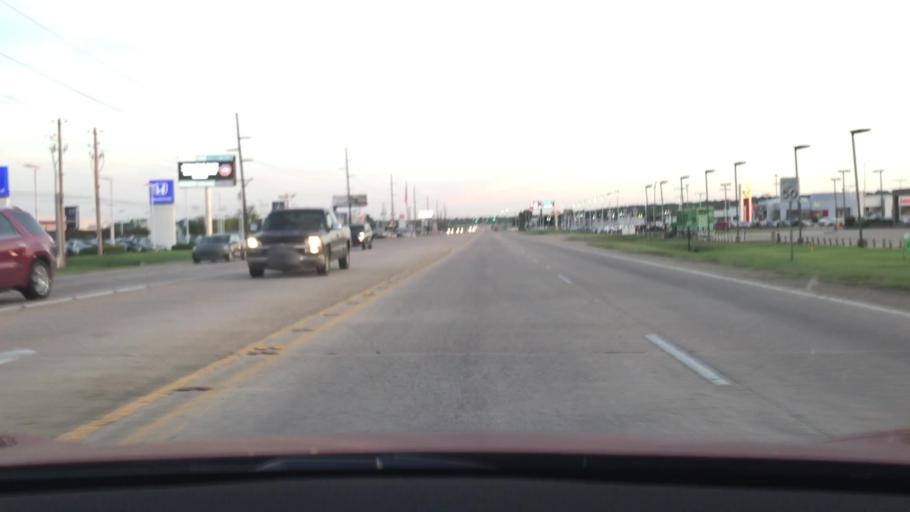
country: US
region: Louisiana
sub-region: Bossier Parish
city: Bossier City
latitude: 32.4233
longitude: -93.7202
